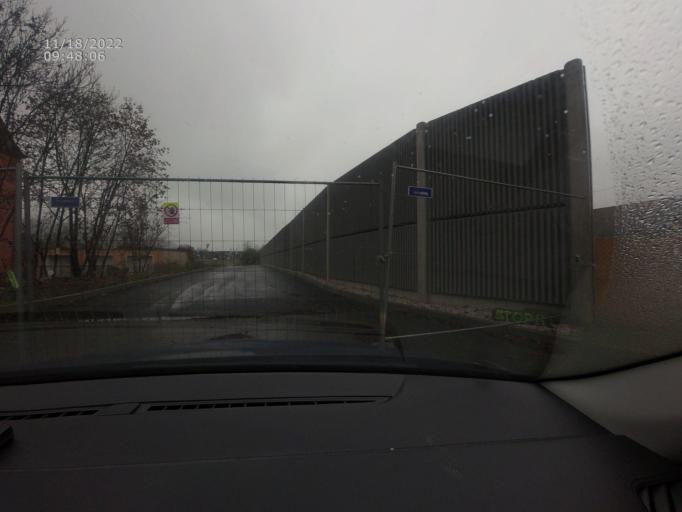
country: CZ
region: Central Bohemia
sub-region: Okres Beroun
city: Beroun
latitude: 49.9582
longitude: 14.0648
